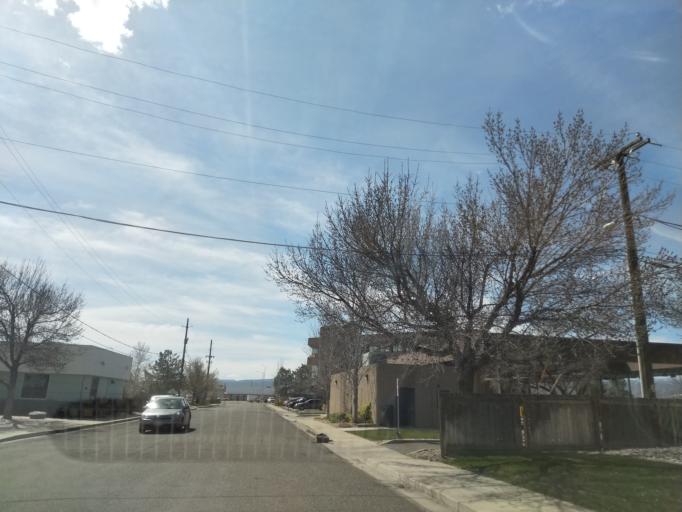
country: US
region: Colorado
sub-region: Mesa County
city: Grand Junction
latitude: 39.0789
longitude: -108.5321
